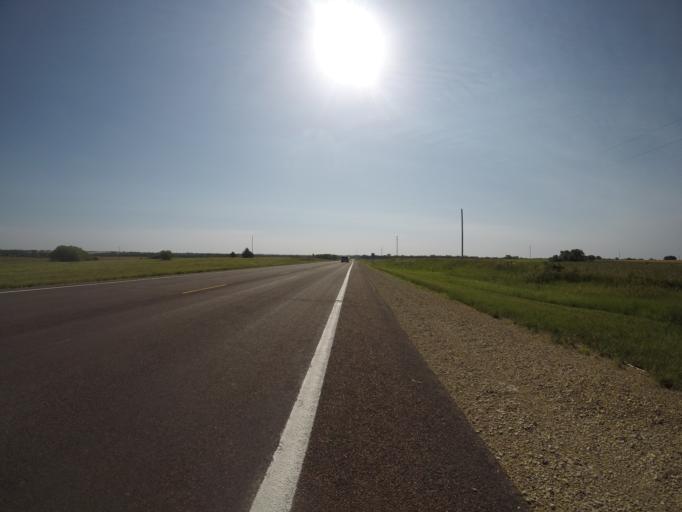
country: US
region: Kansas
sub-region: Riley County
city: Fort Riley North
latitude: 39.3063
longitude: -96.8700
